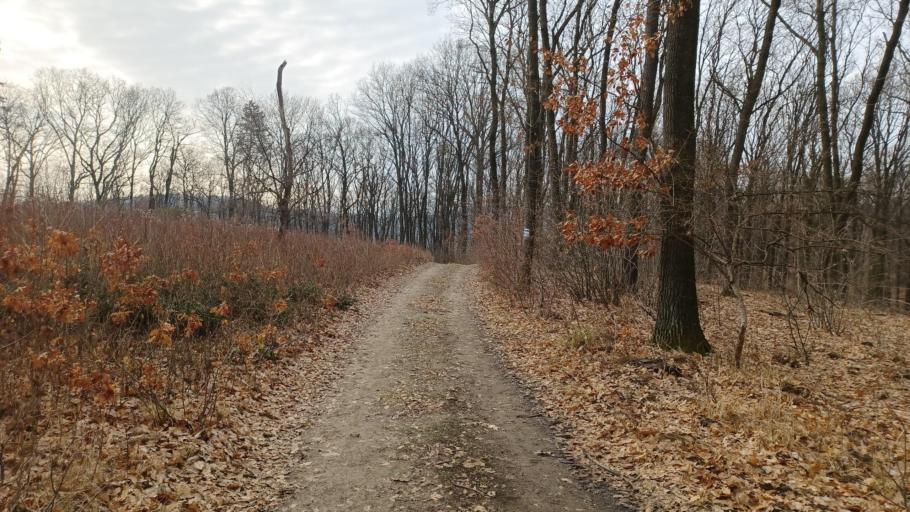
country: HU
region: Tolna
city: Szentgalpuszta
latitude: 46.3358
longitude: 18.6253
